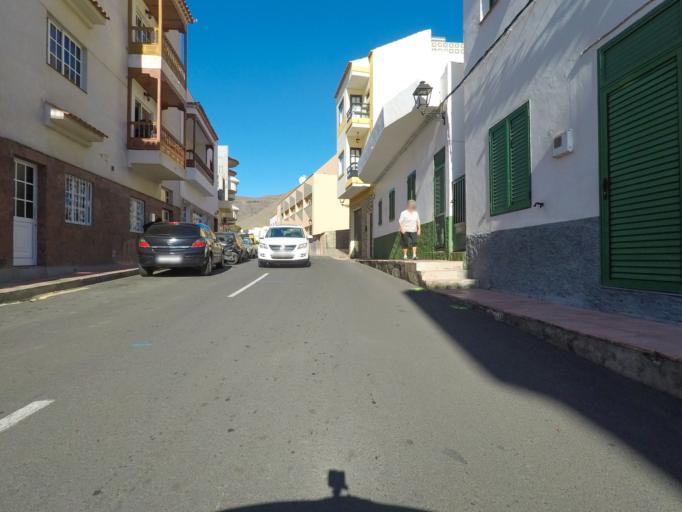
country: ES
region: Canary Islands
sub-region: Provincia de Santa Cruz de Tenerife
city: Alajero
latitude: 28.0307
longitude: -17.1978
